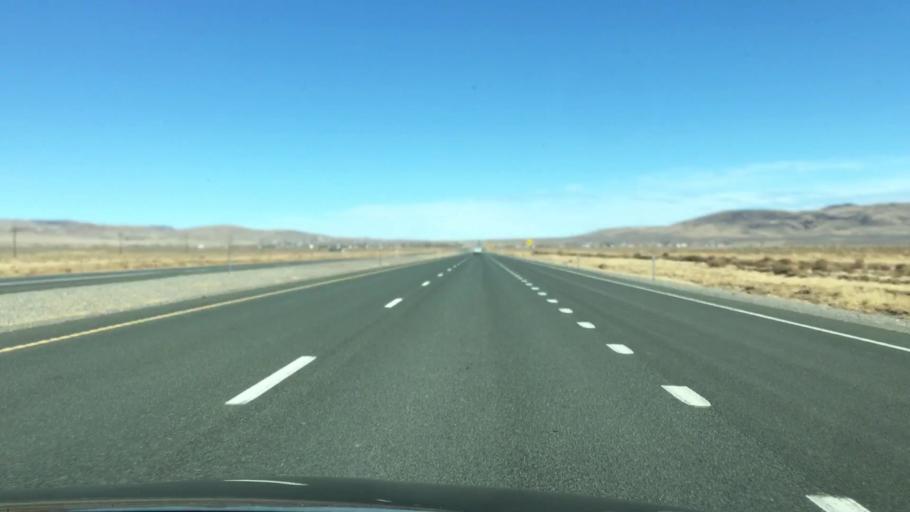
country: US
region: Nevada
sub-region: Lyon County
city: Stagecoach
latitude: 39.3427
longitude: -119.4252
